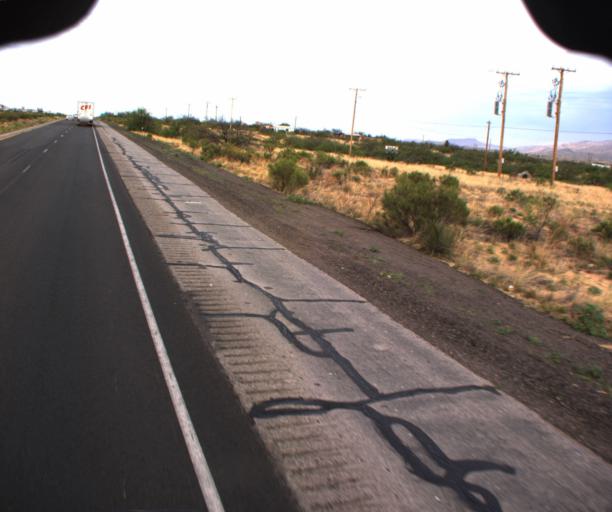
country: US
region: Arizona
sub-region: Cochise County
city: Mescal
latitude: 31.9632
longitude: -110.4061
